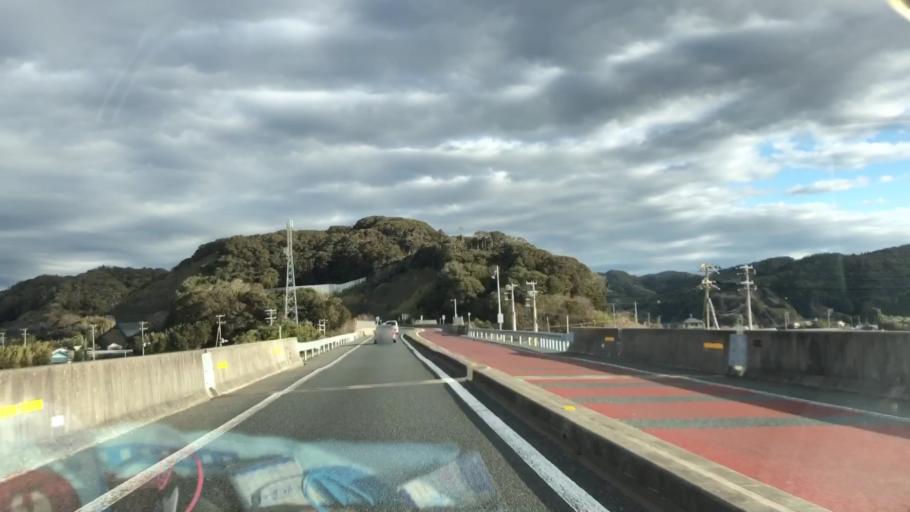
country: JP
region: Chiba
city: Tateyama
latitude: 35.0415
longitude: 139.8514
